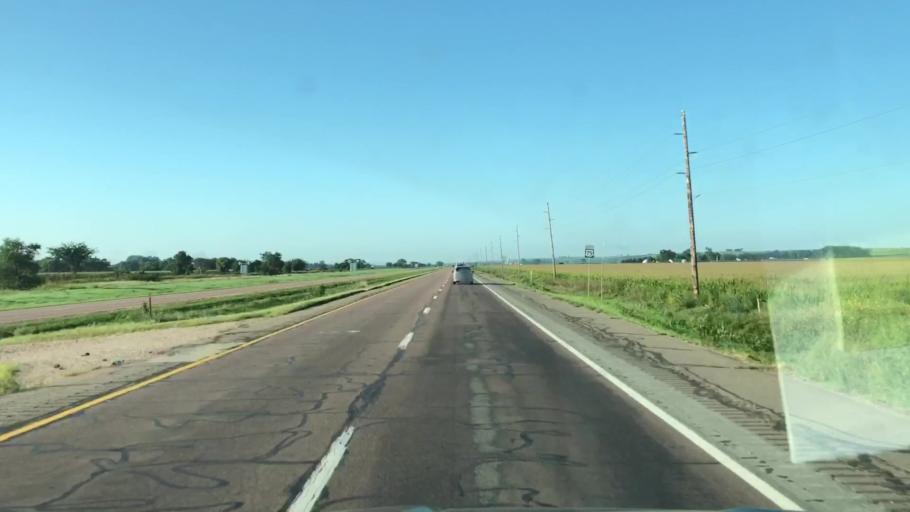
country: US
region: Iowa
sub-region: Plymouth County
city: Le Mars
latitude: 42.7108
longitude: -96.2524
